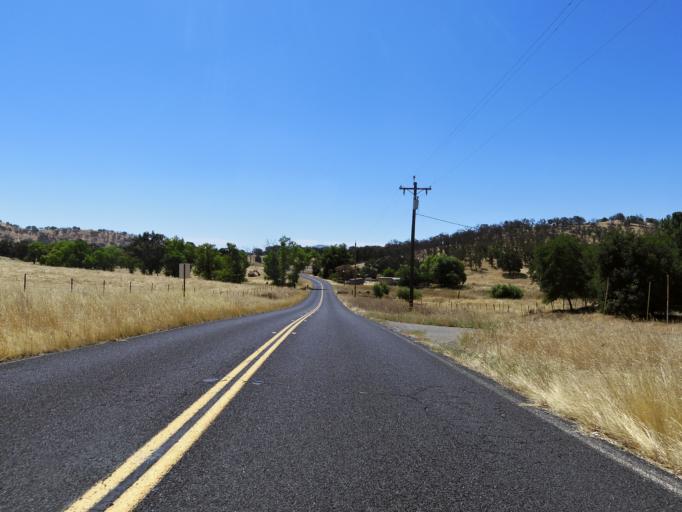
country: US
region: California
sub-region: Merced County
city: Planada
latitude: 37.4985
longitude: -120.2350
